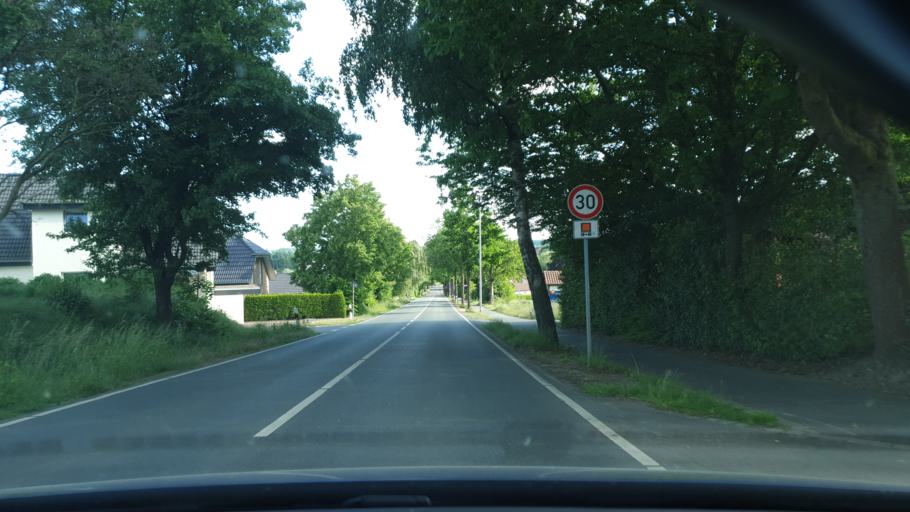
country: DE
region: North Rhine-Westphalia
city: Spenge
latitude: 52.1483
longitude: 8.5149
